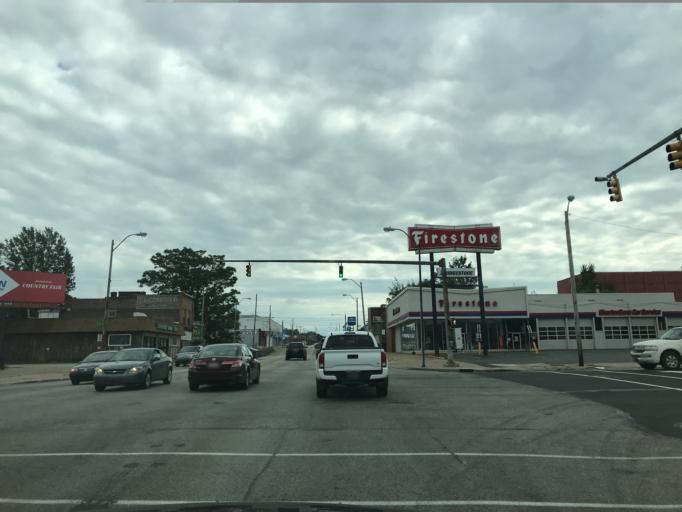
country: US
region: Pennsylvania
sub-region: Erie County
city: Erie
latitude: 42.1187
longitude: -80.0781
